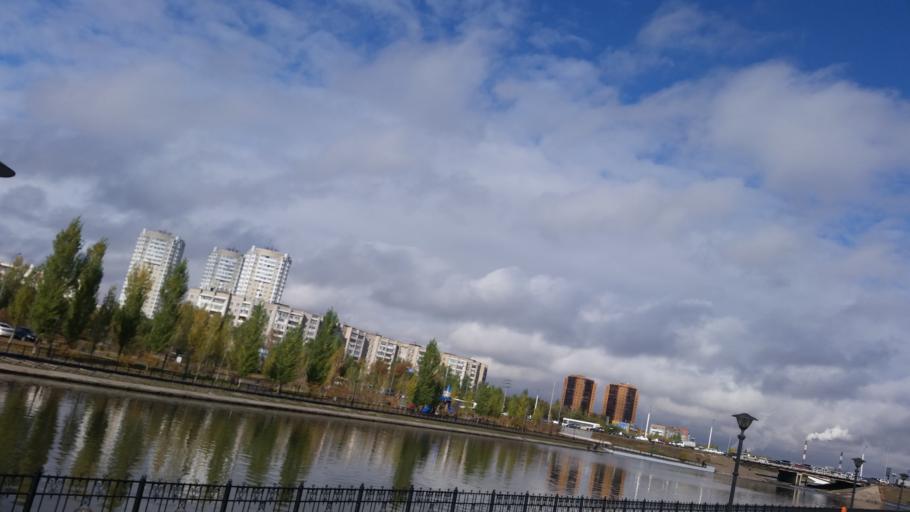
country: KZ
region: Astana Qalasy
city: Astana
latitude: 51.1590
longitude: 71.4677
